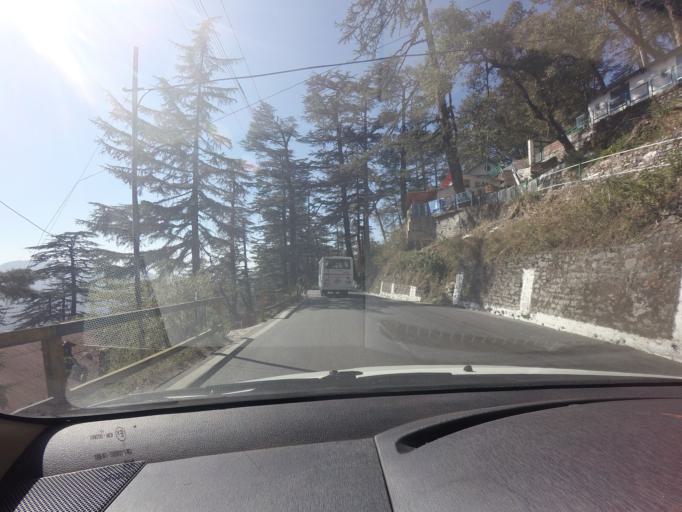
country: IN
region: Himachal Pradesh
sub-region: Shimla
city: Shimla
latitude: 31.1030
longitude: 77.1576
